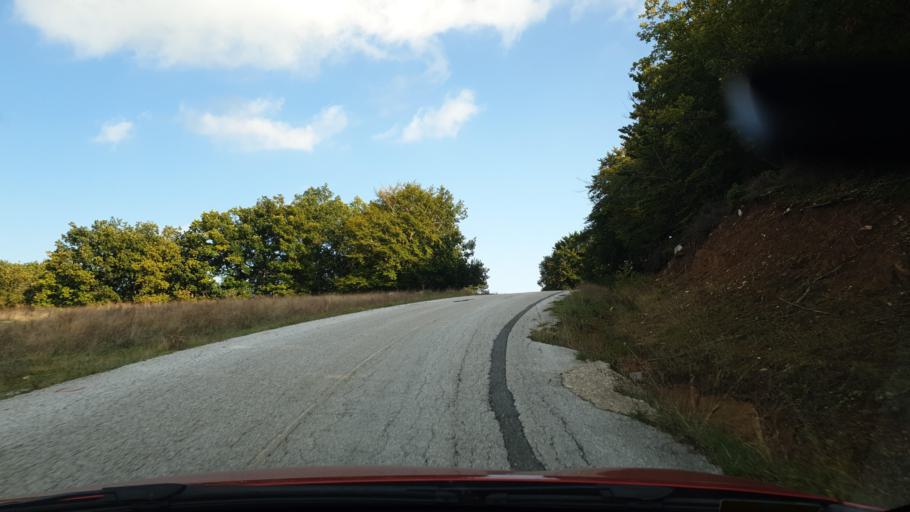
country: GR
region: Central Macedonia
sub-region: Nomos Chalkidikis
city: Galatista
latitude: 40.5028
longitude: 23.2327
